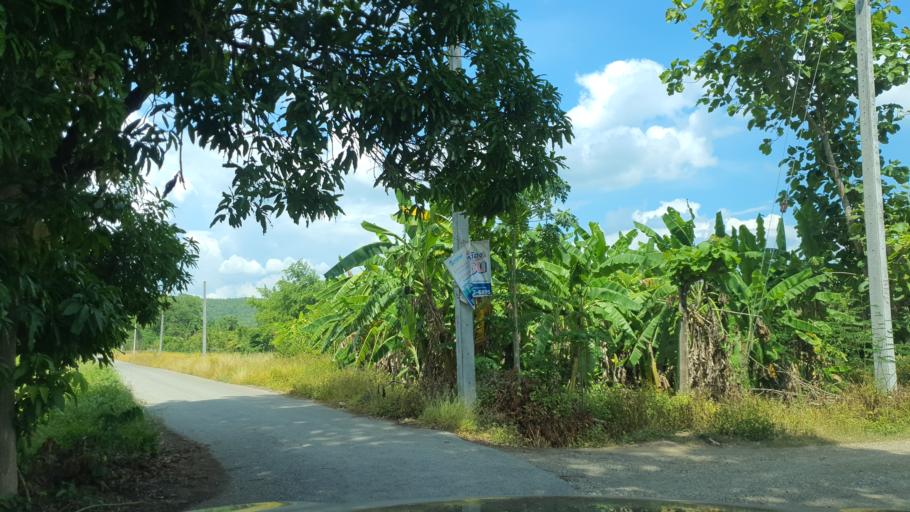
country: TH
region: Chiang Mai
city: Mae Taeng
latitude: 19.0718
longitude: 98.9550
